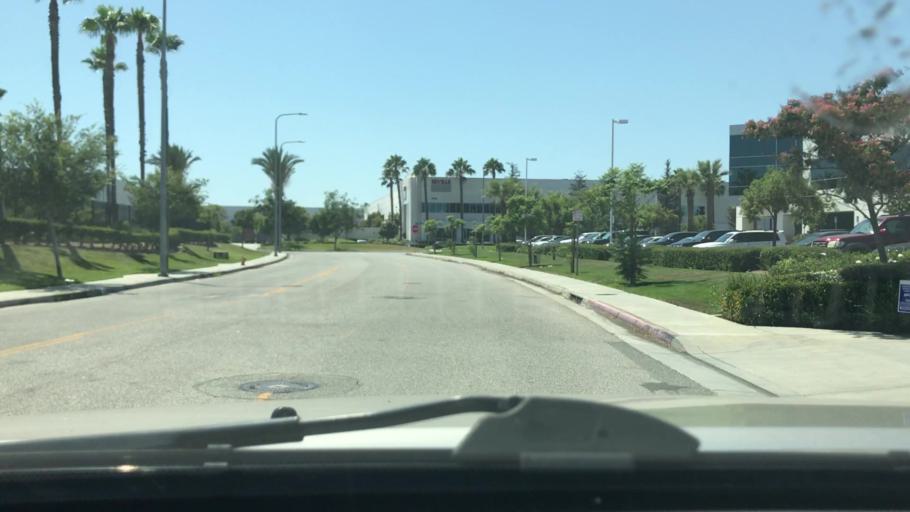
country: US
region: California
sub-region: Los Angeles County
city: Carson
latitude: 33.8542
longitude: -118.3023
